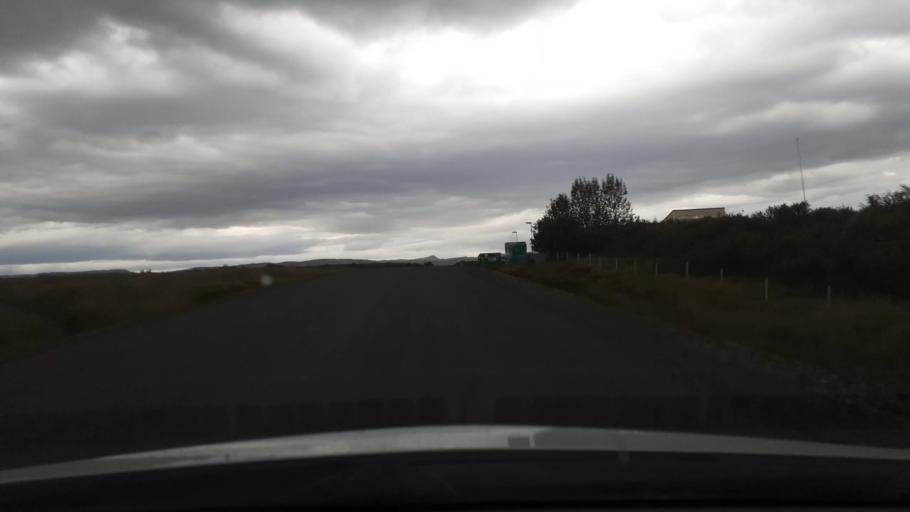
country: IS
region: West
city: Borgarnes
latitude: 64.6733
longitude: -21.7047
